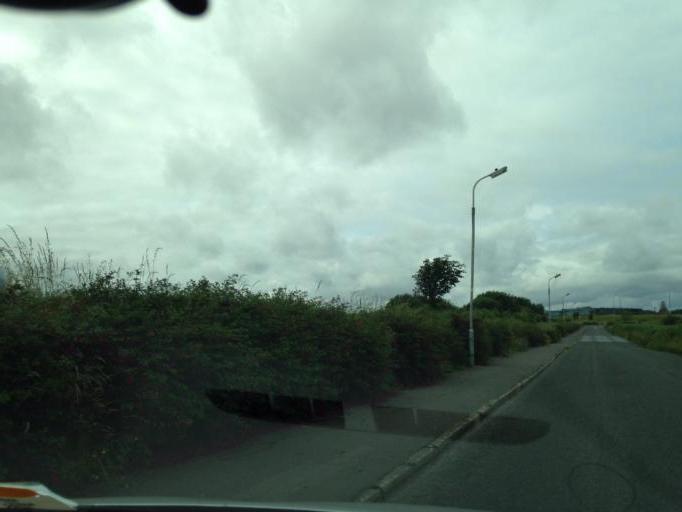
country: IE
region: Connaught
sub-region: County Galway
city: Gaillimh
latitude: 53.2811
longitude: -9.0543
